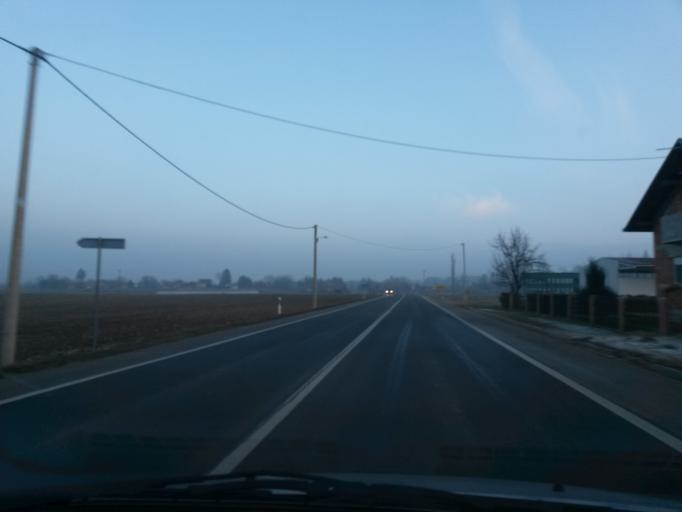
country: HR
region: Varazdinska
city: Ludbreg
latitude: 46.2292
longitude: 16.6645
